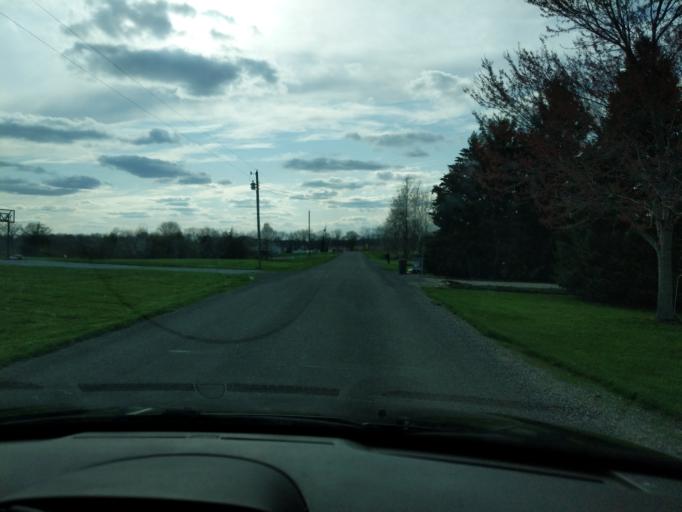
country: US
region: Ohio
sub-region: Champaign County
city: Urbana
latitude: 40.1364
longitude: -83.6850
